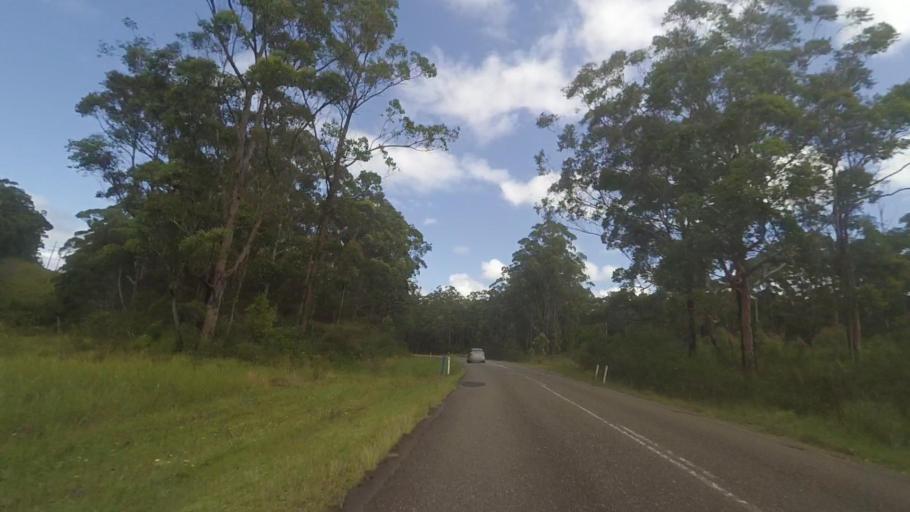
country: AU
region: New South Wales
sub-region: Great Lakes
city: Bulahdelah
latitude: -32.3969
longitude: 152.2535
